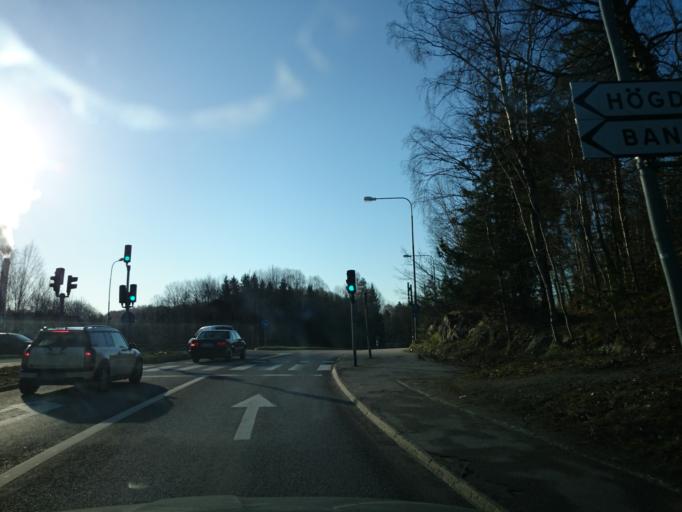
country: SE
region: Stockholm
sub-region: Stockholms Kommun
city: Arsta
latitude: 59.2595
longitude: 18.0444
